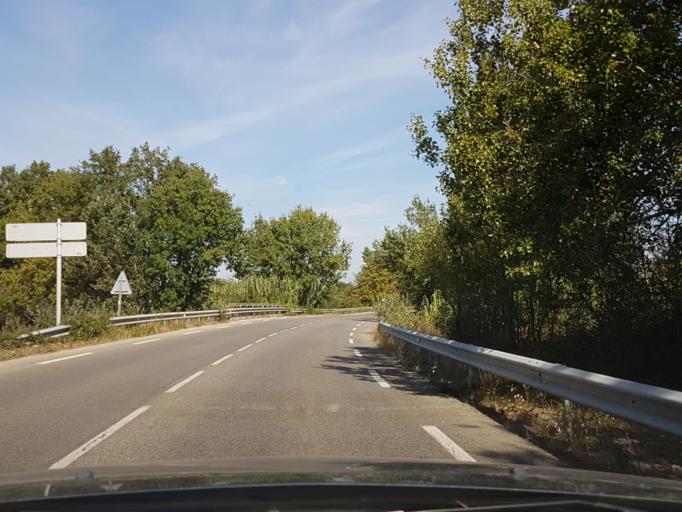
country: FR
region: Provence-Alpes-Cote d'Azur
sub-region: Departement des Bouches-du-Rhone
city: Noves
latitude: 43.8444
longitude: 4.8954
